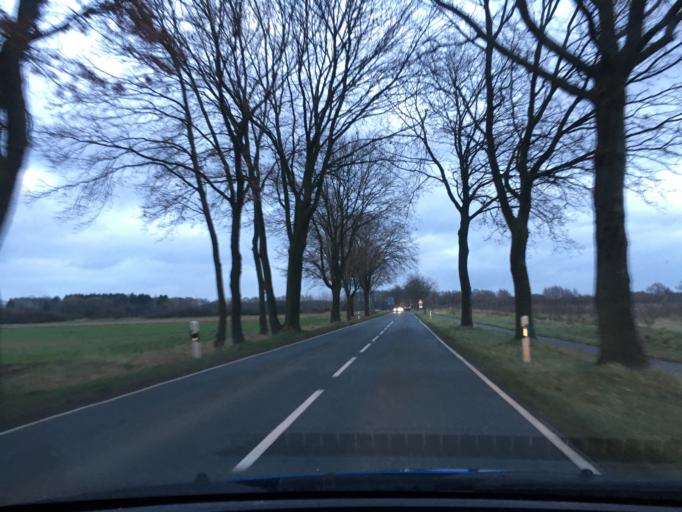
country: DE
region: Lower Saxony
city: Winsen
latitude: 53.3266
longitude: 10.2172
